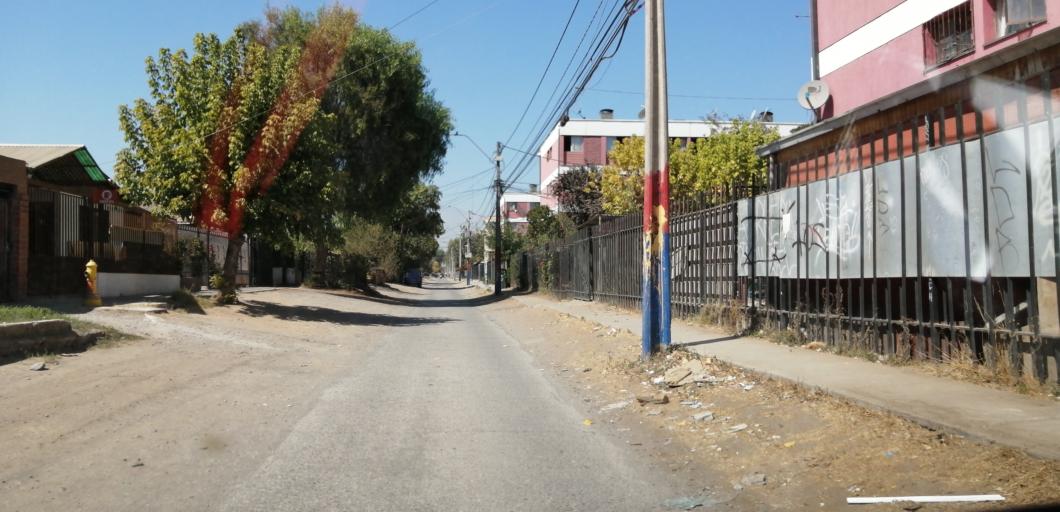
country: CL
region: Santiago Metropolitan
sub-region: Provincia de Santiago
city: Lo Prado
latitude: -33.4500
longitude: -70.7489
